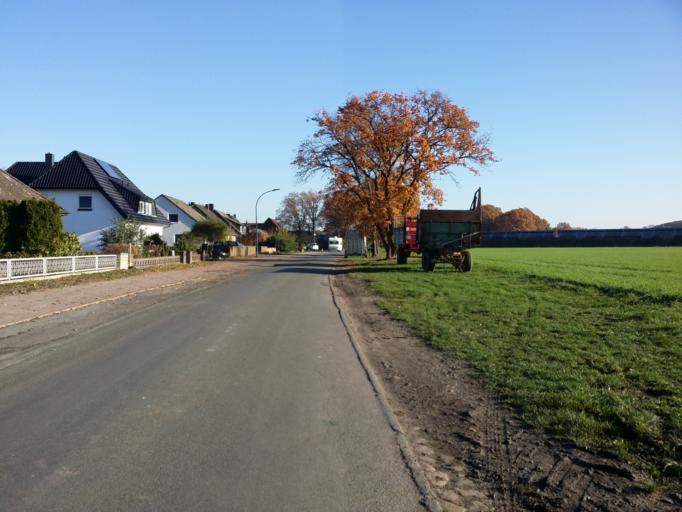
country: DE
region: Lower Saxony
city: Ottersberg
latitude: 53.0620
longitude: 9.0968
